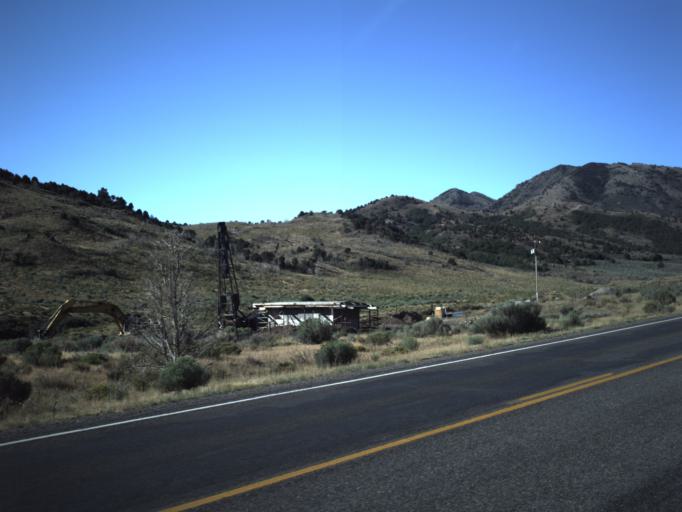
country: US
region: Utah
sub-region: Utah County
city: Genola
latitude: 39.9700
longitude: -112.0873
